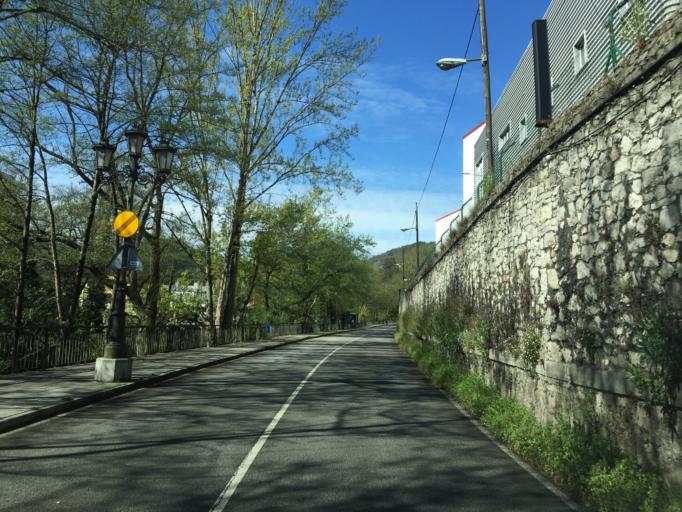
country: ES
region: Asturias
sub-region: Province of Asturias
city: Proaza
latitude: 43.3436
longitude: -5.9757
